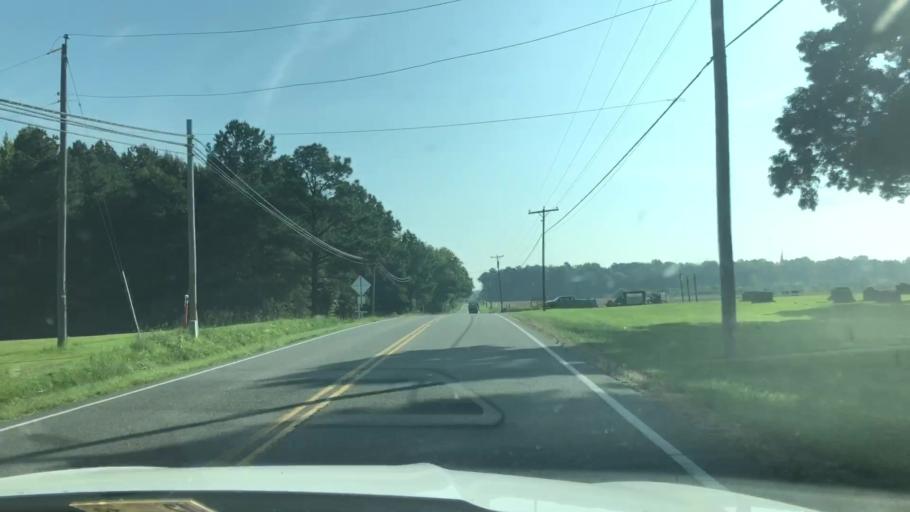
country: US
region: Virginia
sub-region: Richmond County
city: Warsaw
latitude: 37.8899
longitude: -76.6655
